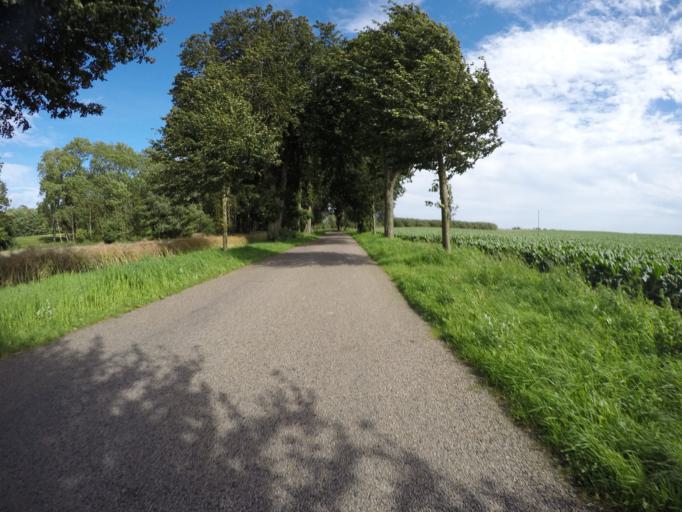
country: SE
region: Skane
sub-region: Simrishamns Kommun
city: Simrishamn
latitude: 55.4997
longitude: 14.2269
